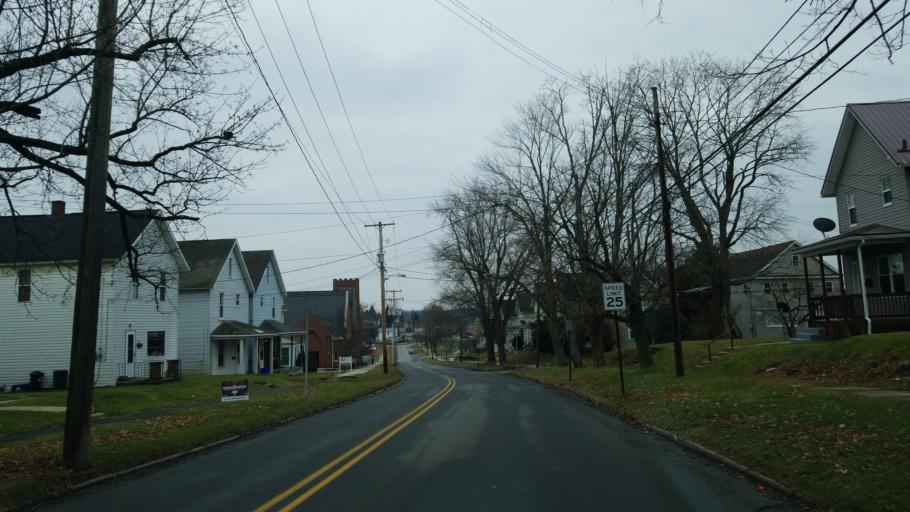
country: US
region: Pennsylvania
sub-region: Clearfield County
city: DuBois
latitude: 41.1339
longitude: -78.7575
